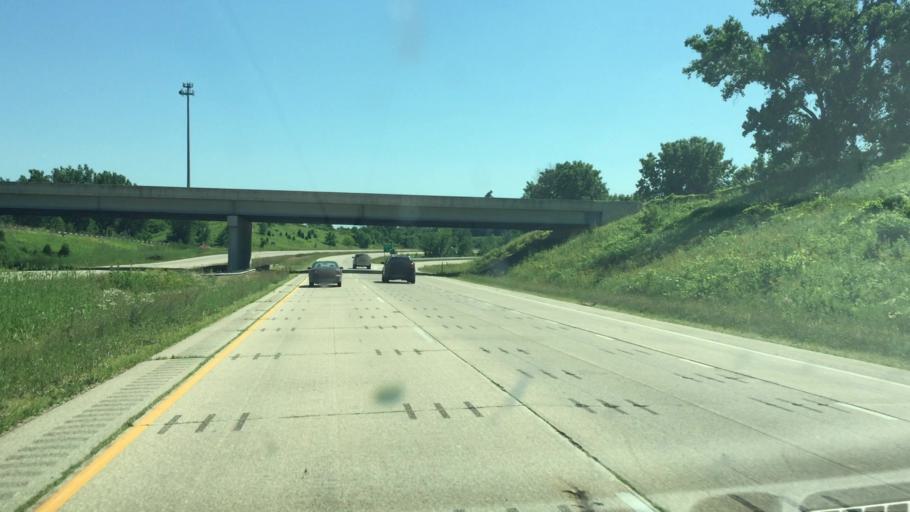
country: US
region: Illinois
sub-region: Jo Daviess County
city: East Dubuque
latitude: 42.5215
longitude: -90.6148
